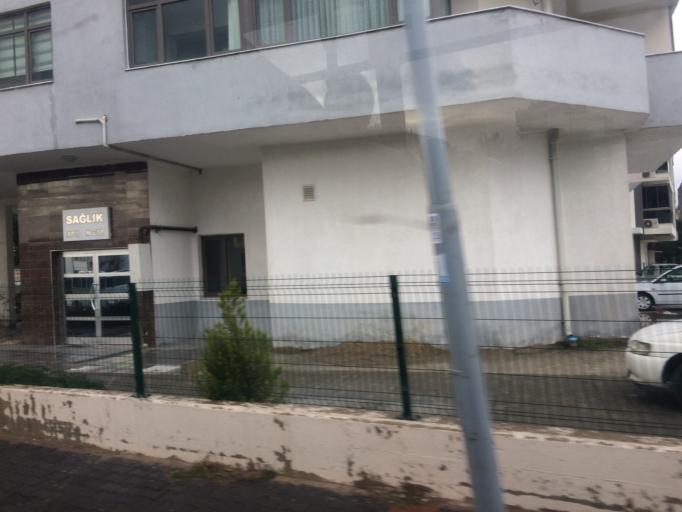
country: TR
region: Izmir
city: Karsiyaka
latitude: 38.4894
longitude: 27.0550
